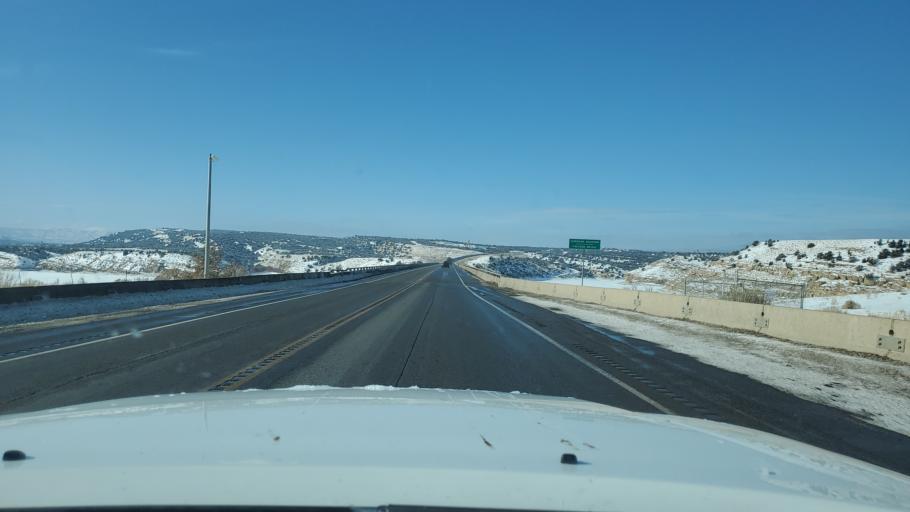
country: US
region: Utah
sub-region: Duchesne County
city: Duchesne
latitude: 40.1733
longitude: -110.4934
